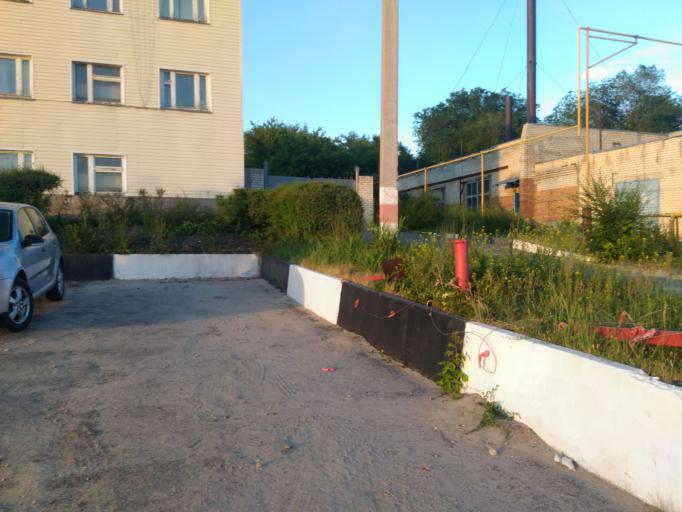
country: RU
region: Ulyanovsk
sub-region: Ulyanovskiy Rayon
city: Ulyanovsk
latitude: 54.3353
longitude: 48.3641
